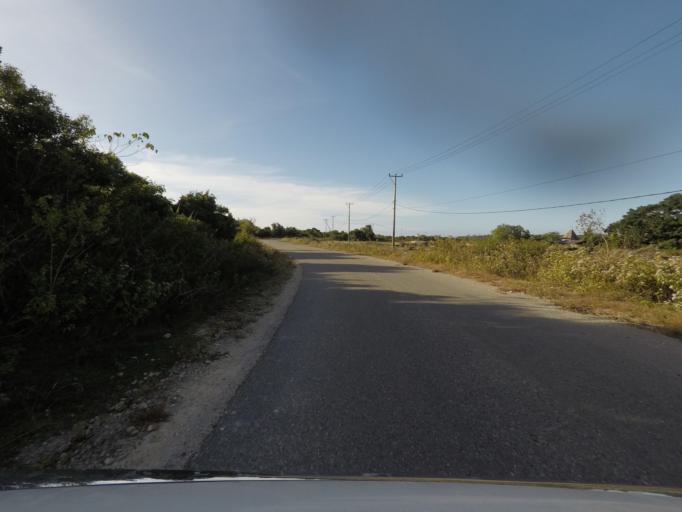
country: TL
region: Lautem
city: Lospalos
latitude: -8.3908
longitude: 127.0104
